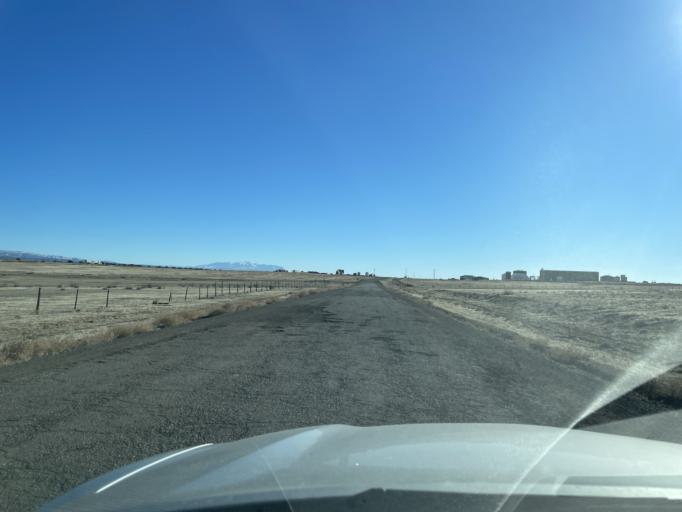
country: US
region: Colorado
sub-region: Mesa County
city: Loma
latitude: 39.1780
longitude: -109.1314
